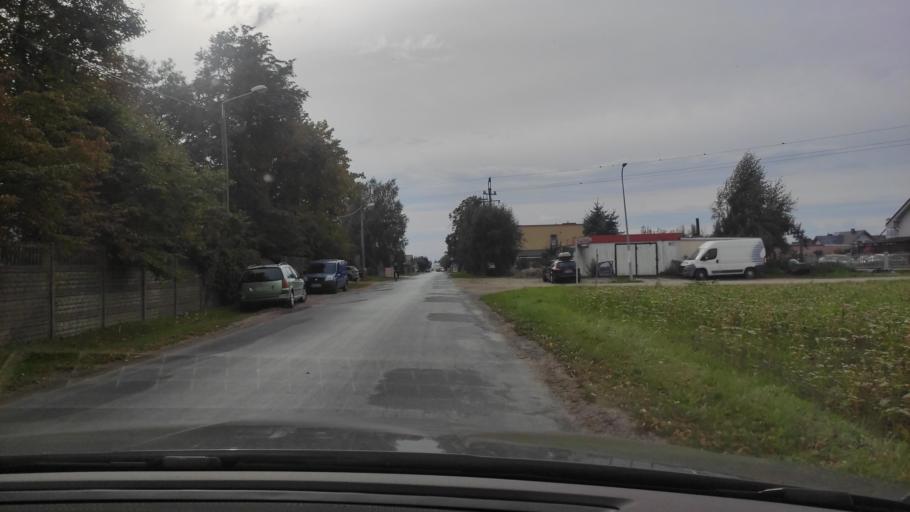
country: PL
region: Greater Poland Voivodeship
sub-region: Powiat poznanski
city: Kleszczewo
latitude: 52.3648
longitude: 17.1380
